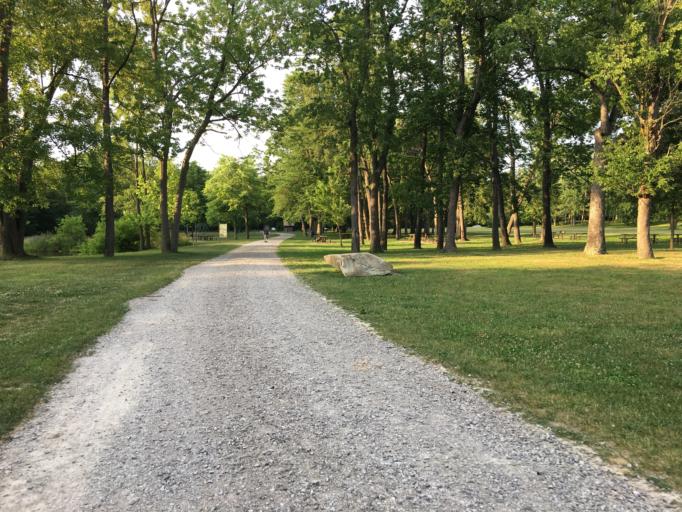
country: US
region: Ohio
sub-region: Cuyahoga County
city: Berea
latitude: 41.3620
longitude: -81.8593
